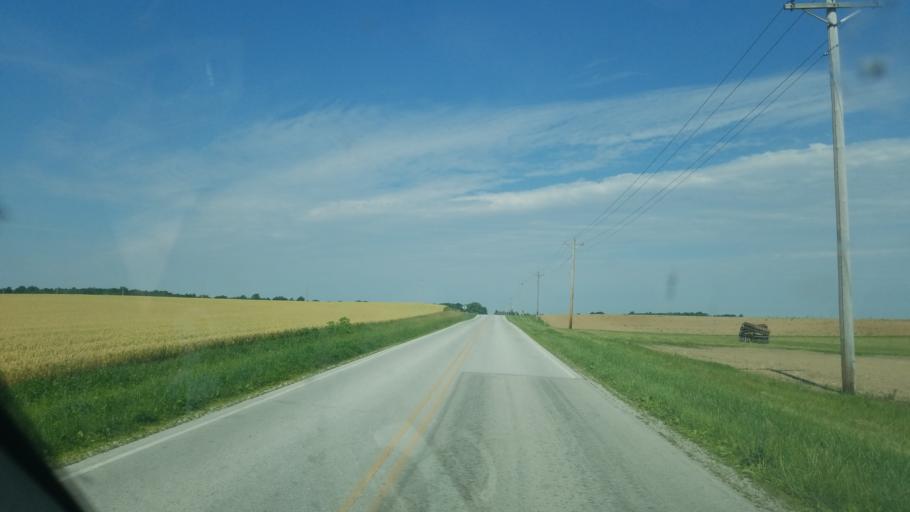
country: US
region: Ohio
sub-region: Wyandot County
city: Carey
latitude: 40.9637
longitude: -83.2753
